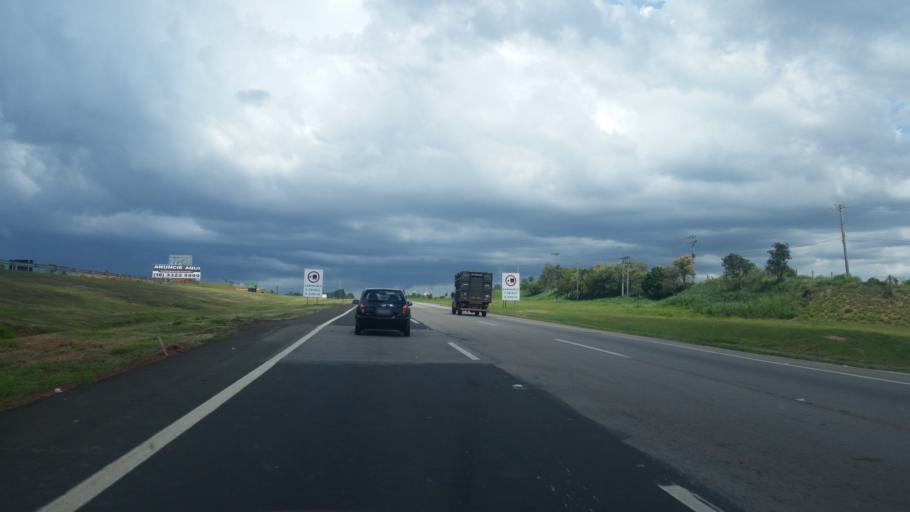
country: BR
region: Sao Paulo
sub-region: Boituva
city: Boituva
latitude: -23.2904
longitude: -47.7459
